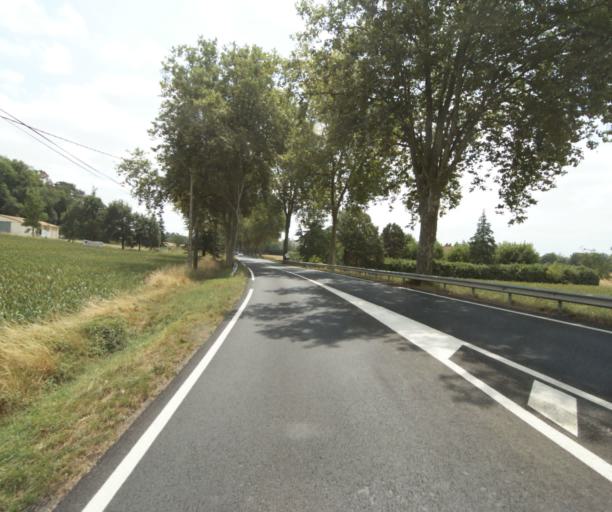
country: FR
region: Midi-Pyrenees
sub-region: Departement de la Haute-Garonne
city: Revel
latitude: 43.4445
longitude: 1.9516
